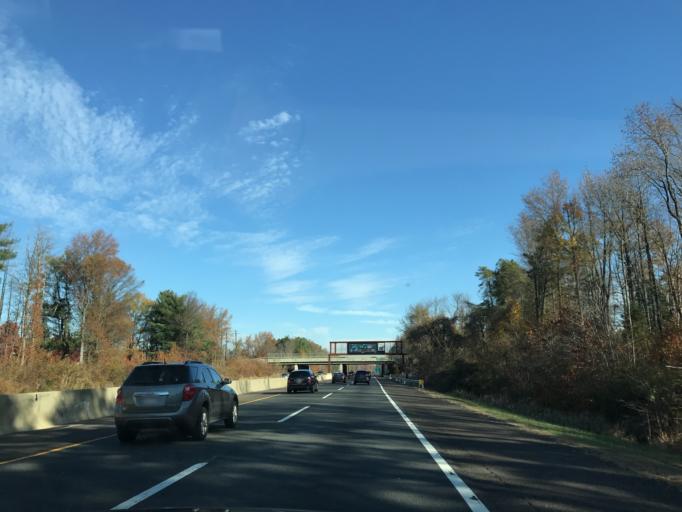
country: US
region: New Jersey
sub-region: Camden County
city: Springdale
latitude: 39.9054
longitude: -74.9817
